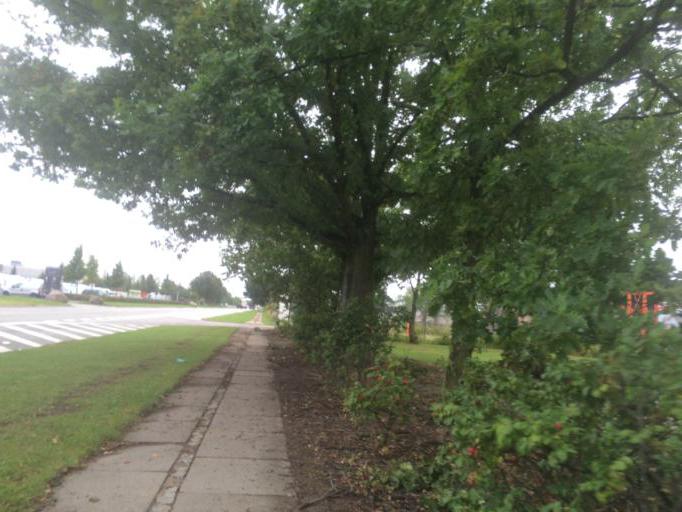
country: DK
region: Capital Region
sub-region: Hvidovre Kommune
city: Hvidovre
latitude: 55.6126
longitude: 12.4832
